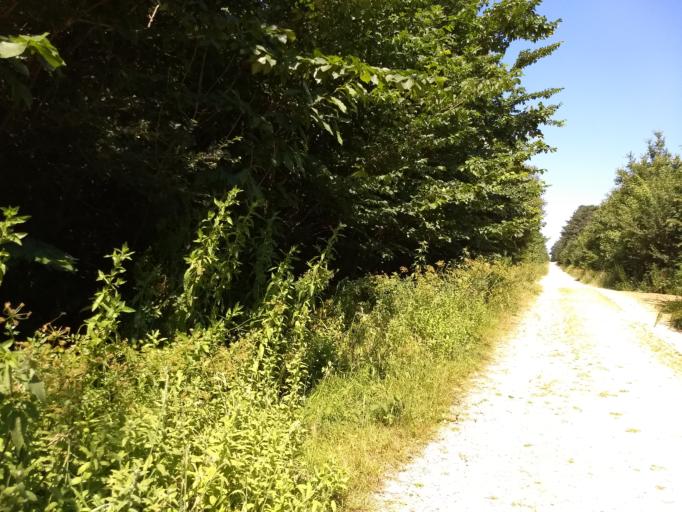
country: GB
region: England
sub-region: Isle of Wight
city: Northwood
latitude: 50.7058
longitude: -1.3315
